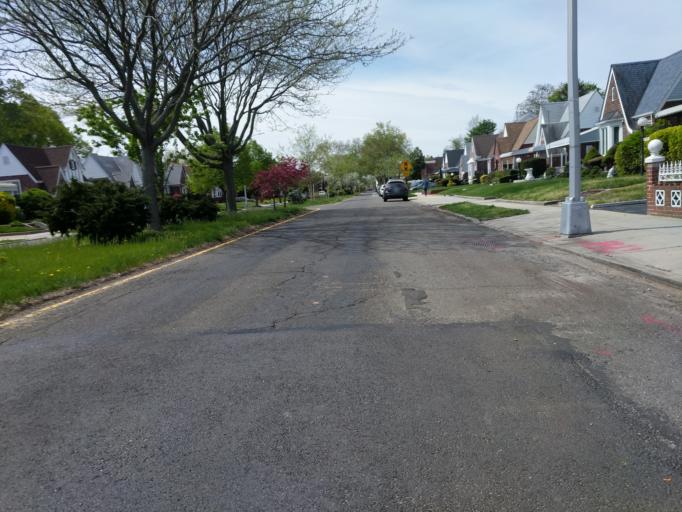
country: US
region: New York
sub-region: Nassau County
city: South Valley Stream
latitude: 40.6786
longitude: -73.7382
